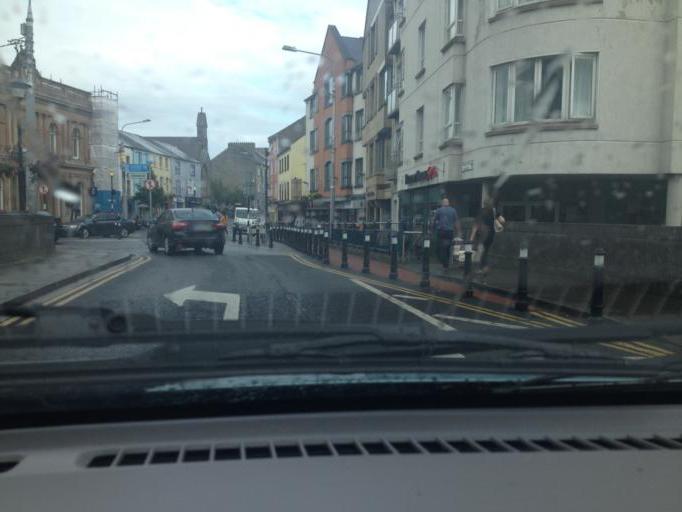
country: IE
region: Connaught
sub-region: Sligo
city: Sligo
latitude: 54.2723
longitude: -8.4744
